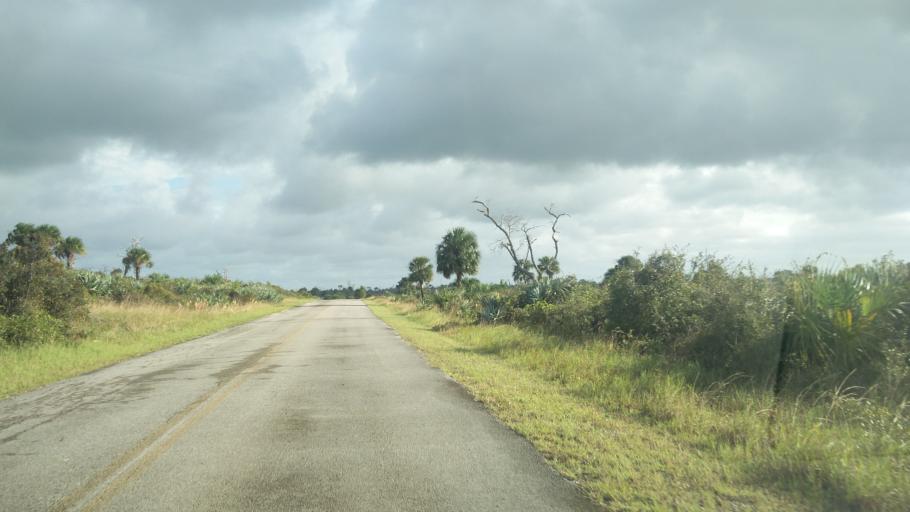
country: US
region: Florida
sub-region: Palm Beach County
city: Tequesta
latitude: 27.0128
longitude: -80.1088
